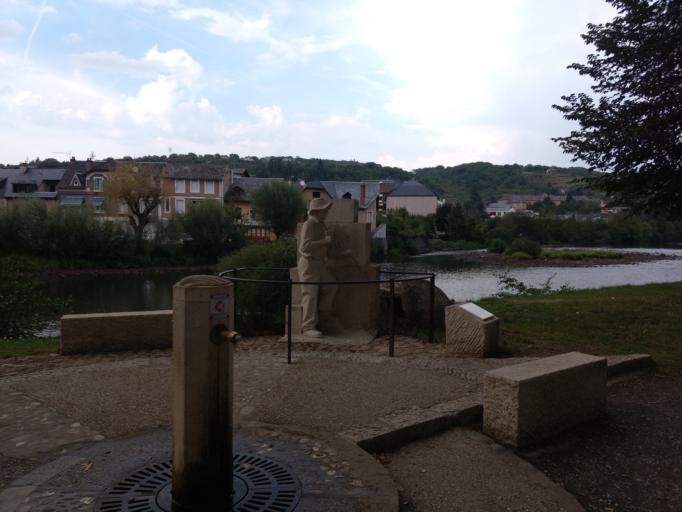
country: FR
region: Midi-Pyrenees
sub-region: Departement de l'Aveyron
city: Espalion
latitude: 44.5211
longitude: 2.7651
